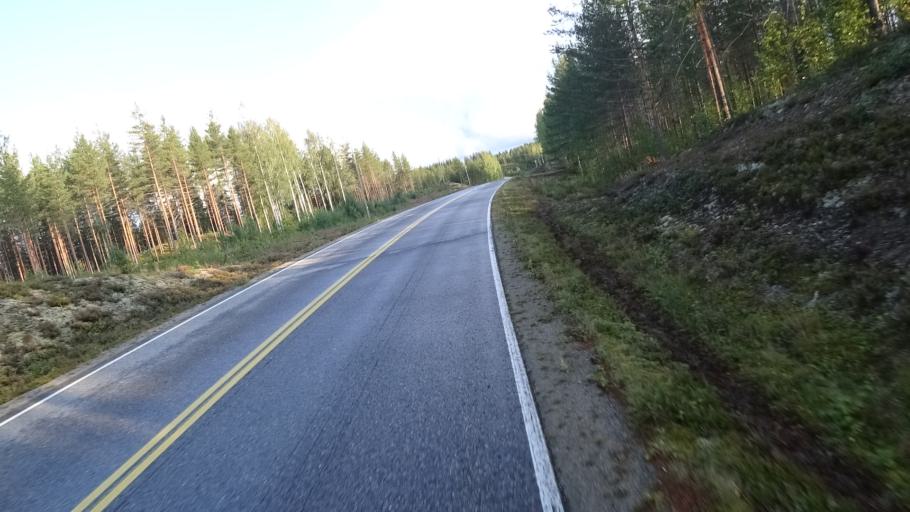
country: FI
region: North Karelia
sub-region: Joensuu
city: Ilomantsi
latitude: 62.6334
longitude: 31.0930
